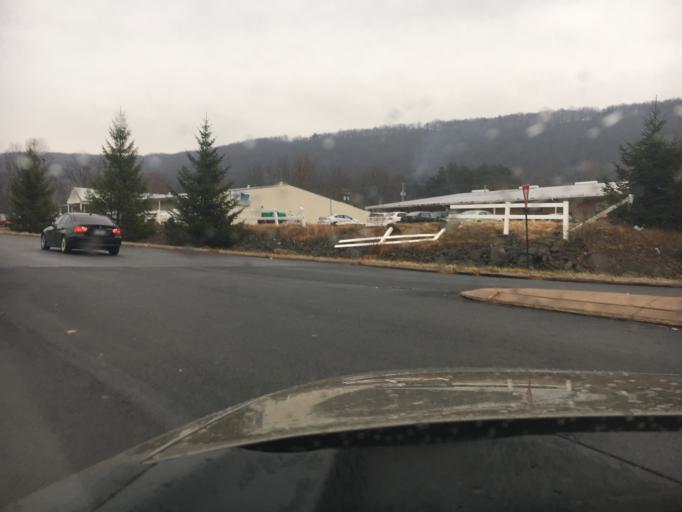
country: US
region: Pennsylvania
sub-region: Luzerne County
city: Harleigh
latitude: 41.0109
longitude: -75.9657
